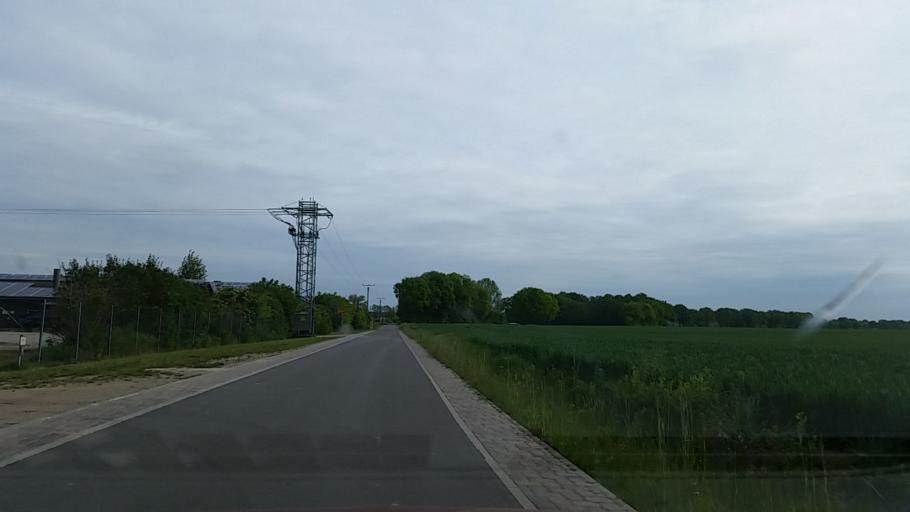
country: DE
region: Lower Saxony
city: Luder
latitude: 52.7520
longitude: 10.6798
